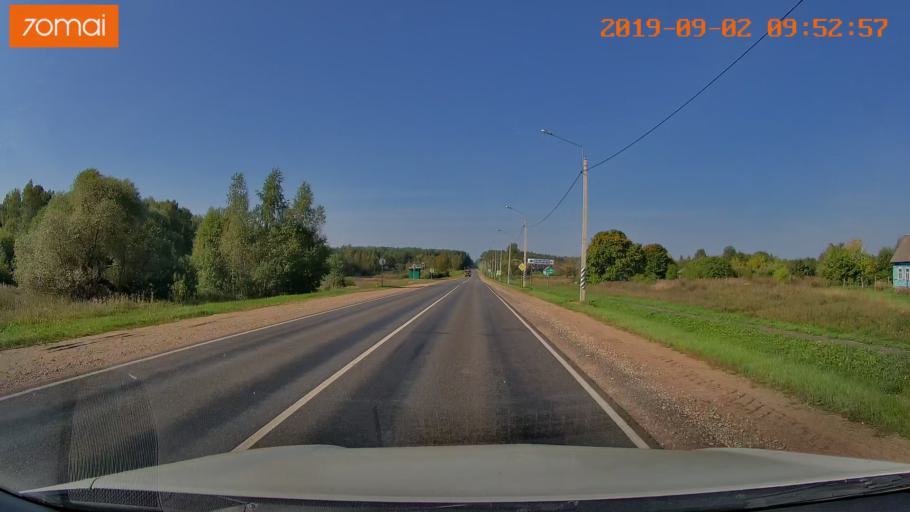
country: RU
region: Kaluga
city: Mosal'sk
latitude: 54.5865
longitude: 34.6841
